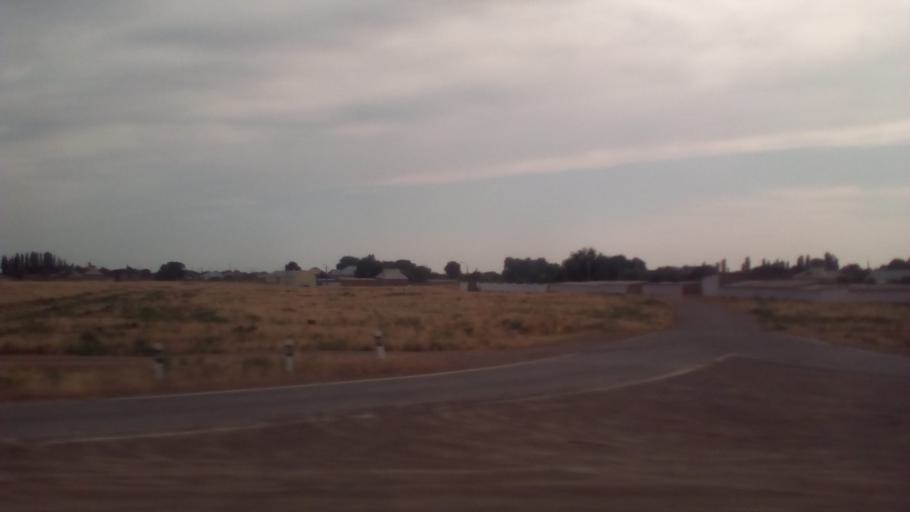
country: KZ
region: Ongtustik Qazaqstan
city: Temirlanovka
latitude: 42.7932
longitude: 69.2039
